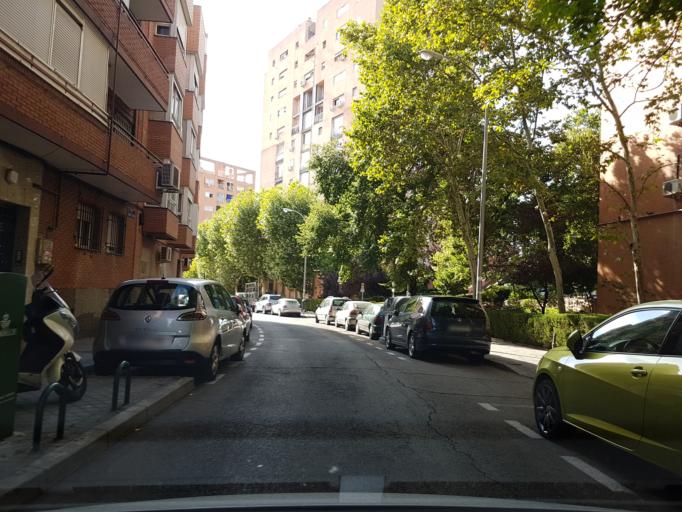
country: ES
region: Madrid
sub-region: Provincia de Madrid
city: Puente de Vallecas
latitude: 40.4051
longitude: -3.6612
